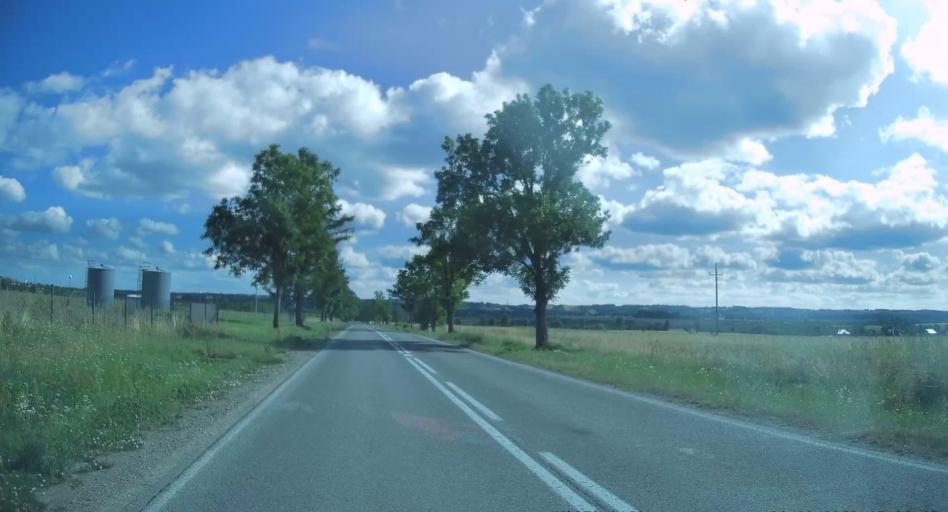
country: PL
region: Swietokrzyskie
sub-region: Powiat kielecki
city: Lagow
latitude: 50.7914
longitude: 21.0815
